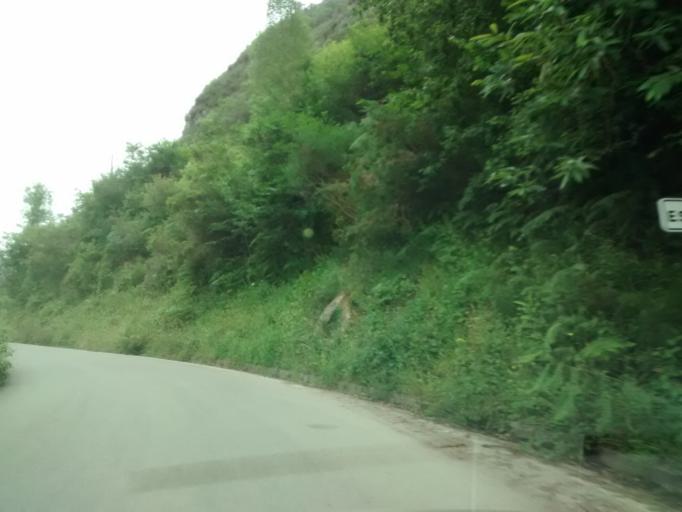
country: ES
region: Asturias
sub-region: Province of Asturias
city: Pilona
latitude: 43.3077
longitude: -5.3633
